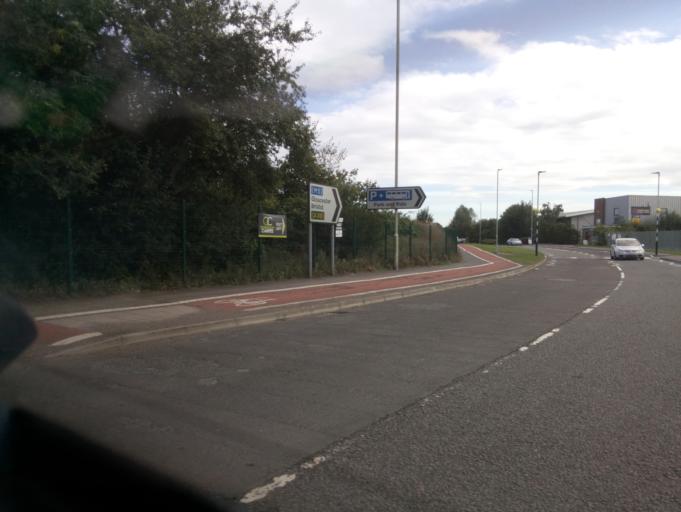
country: GB
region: England
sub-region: Gloucestershire
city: Gloucester
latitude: 51.8166
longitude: -2.2770
